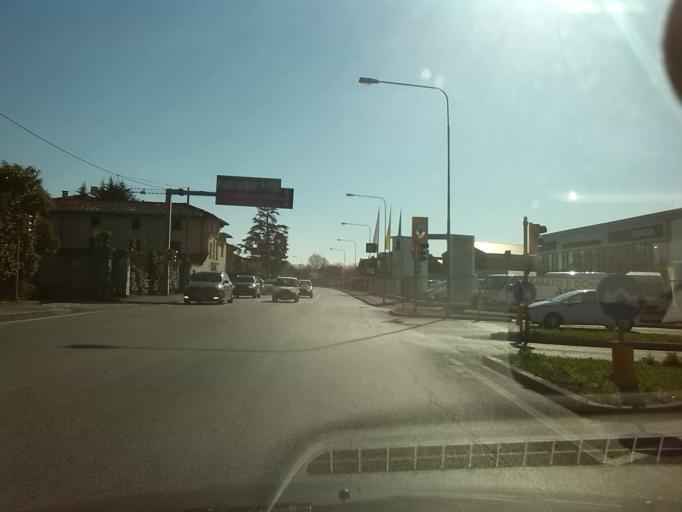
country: IT
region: Friuli Venezia Giulia
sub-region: Provincia di Udine
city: Udine
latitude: 46.0758
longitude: 13.2792
